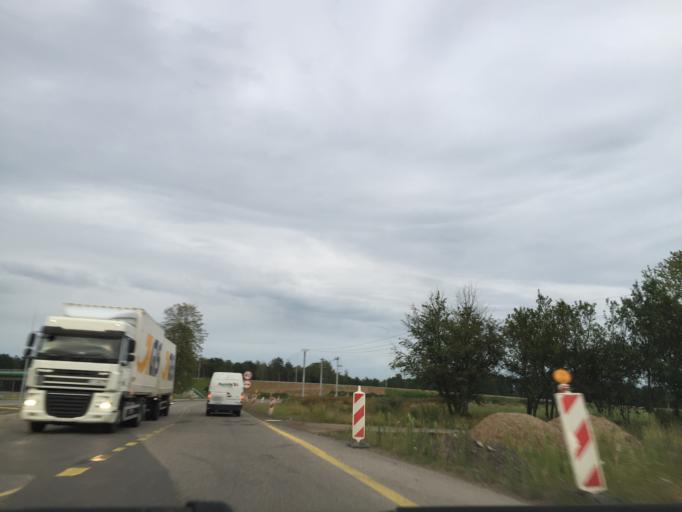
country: PL
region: Podlasie
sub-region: Powiat bialostocki
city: Tykocin
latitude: 53.1244
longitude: 22.6770
